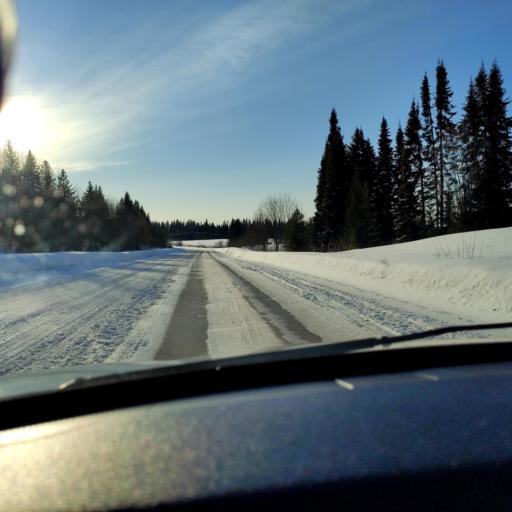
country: RU
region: Perm
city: Polazna
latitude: 58.3441
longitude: 56.4522
